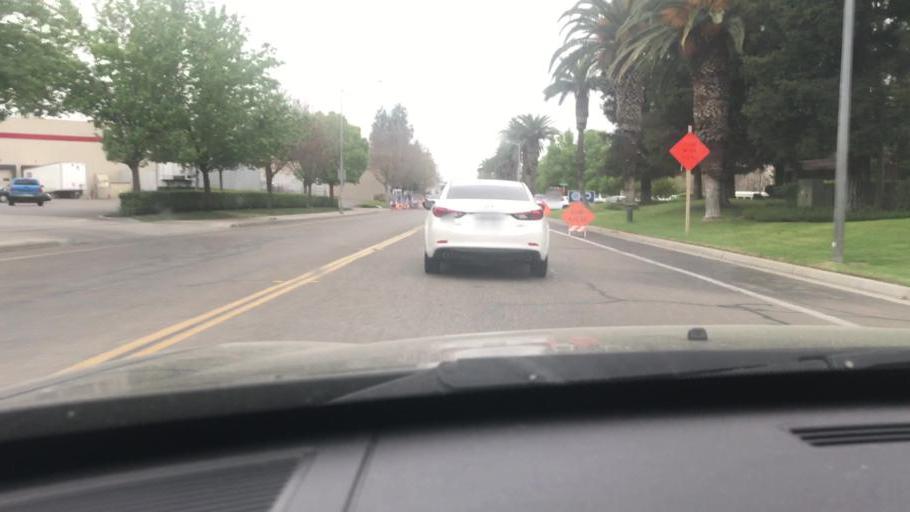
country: US
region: California
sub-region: Fresno County
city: West Park
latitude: 36.8115
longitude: -119.8737
